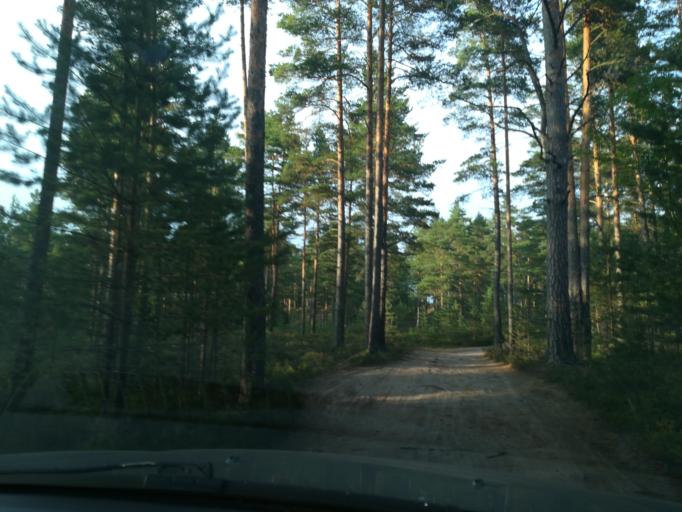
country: RU
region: Leningrad
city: Ust'-Luga
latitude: 59.6778
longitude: 28.2334
